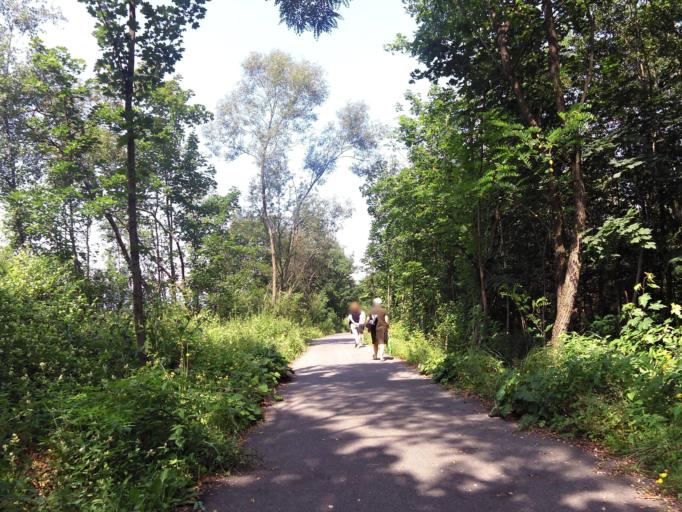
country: PL
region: Silesian Voivodeship
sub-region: Powiat zywiecki
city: Milowka
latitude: 49.5370
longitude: 19.1086
